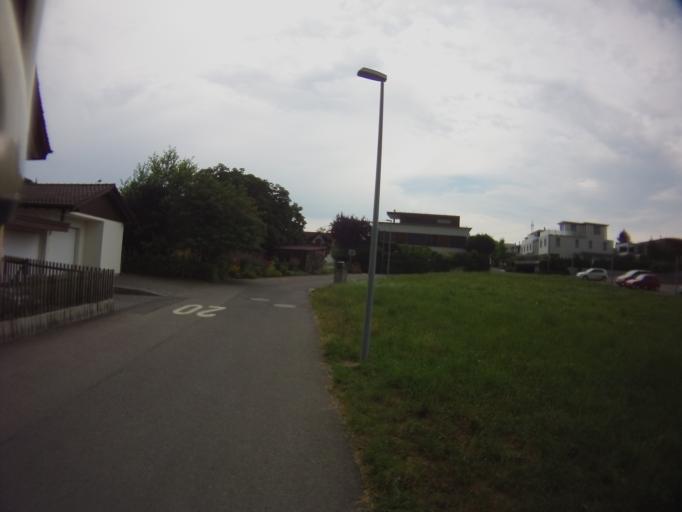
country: CH
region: Zug
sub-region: Zug
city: Hunenberg
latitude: 47.1774
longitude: 8.4256
